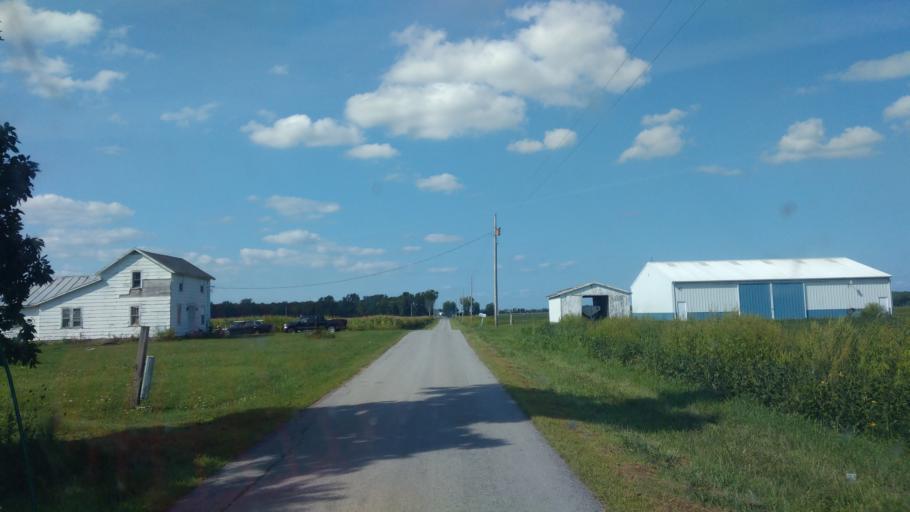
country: US
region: Ohio
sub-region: Hardin County
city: Forest
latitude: 40.7195
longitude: -83.4779
